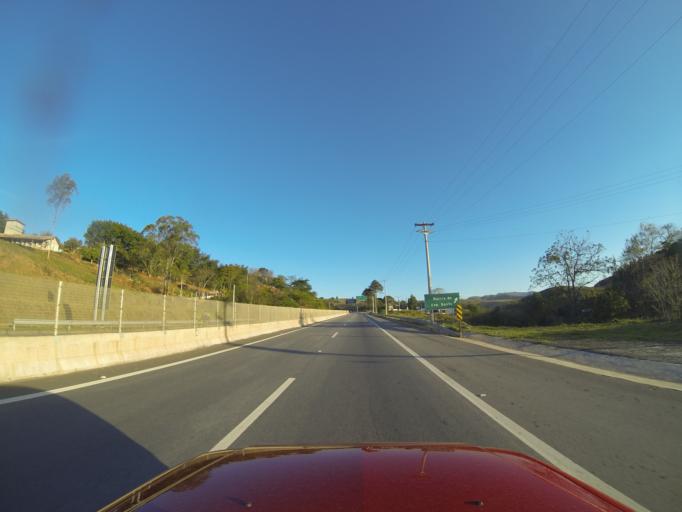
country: BR
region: Sao Paulo
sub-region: Santa Branca
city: Santa Branca
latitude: -23.4164
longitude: -45.6395
